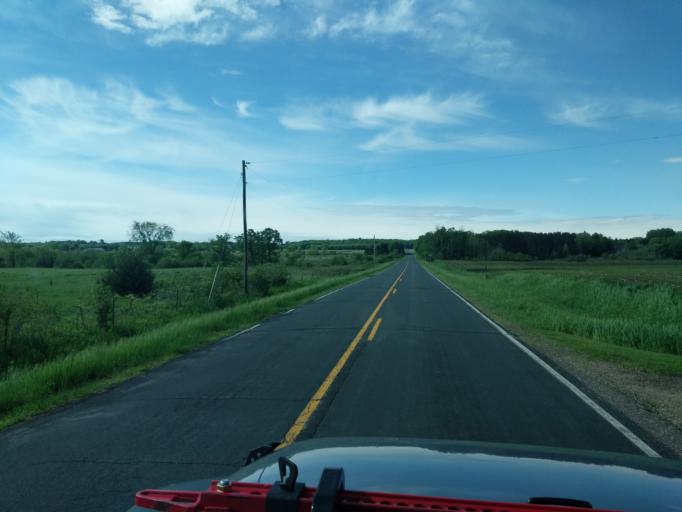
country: US
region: Wisconsin
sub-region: Saint Croix County
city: Hammond
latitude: 44.8972
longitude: -92.4865
